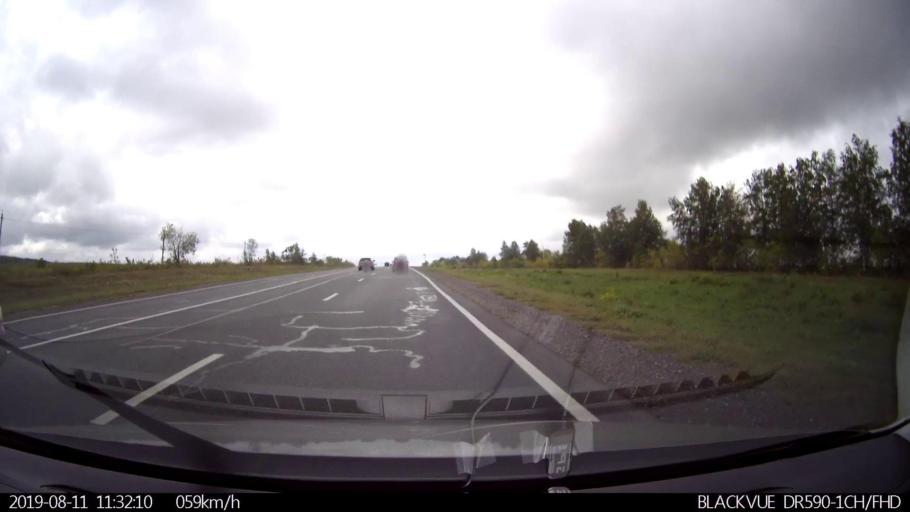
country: RU
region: Ulyanovsk
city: Krasnyy Gulyay
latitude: 54.0403
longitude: 48.2138
